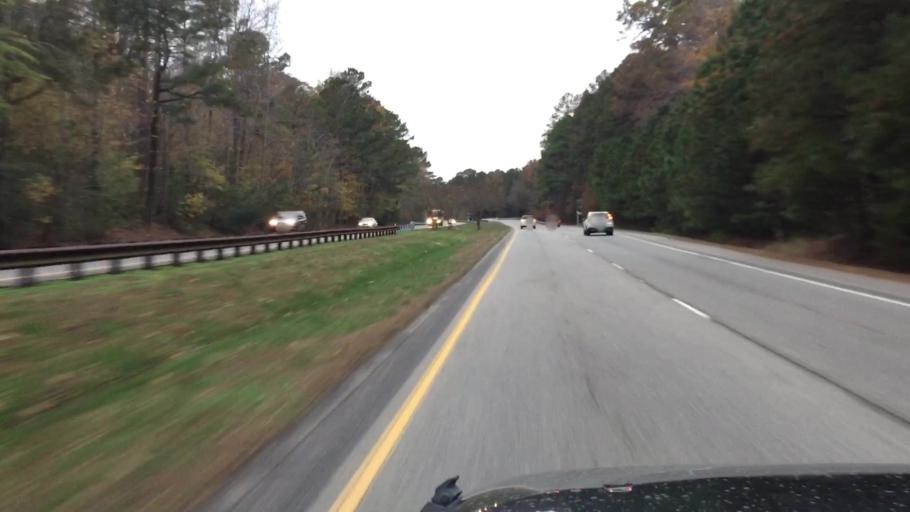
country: US
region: Virginia
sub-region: City of Williamsburg
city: Williamsburg
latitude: 37.2483
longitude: -76.6939
